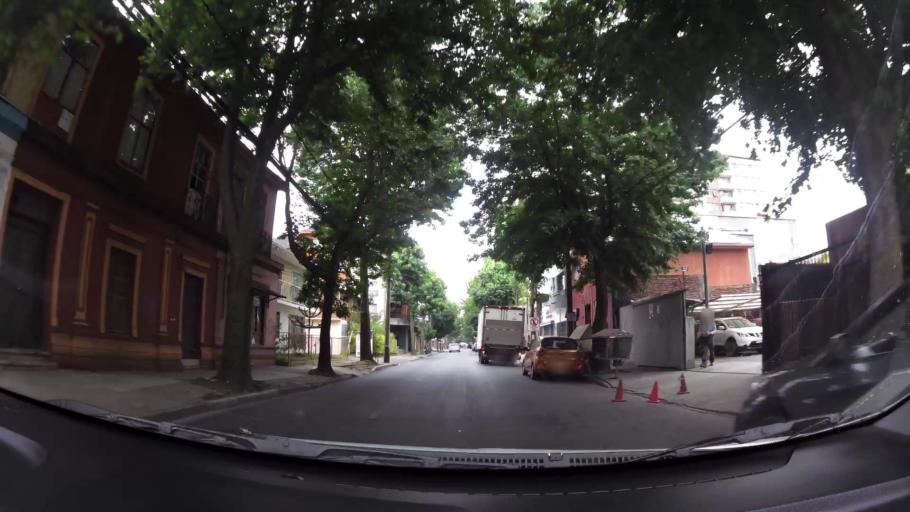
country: CL
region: Biobio
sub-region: Provincia de Concepcion
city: Concepcion
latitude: -36.8201
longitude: -73.0381
